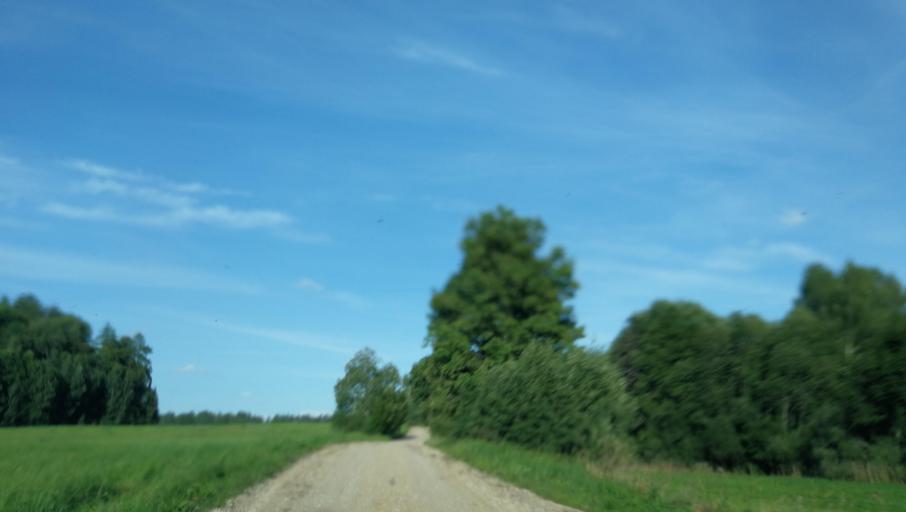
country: LV
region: Amatas Novads
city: Drabesi
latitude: 57.2573
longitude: 25.2974
